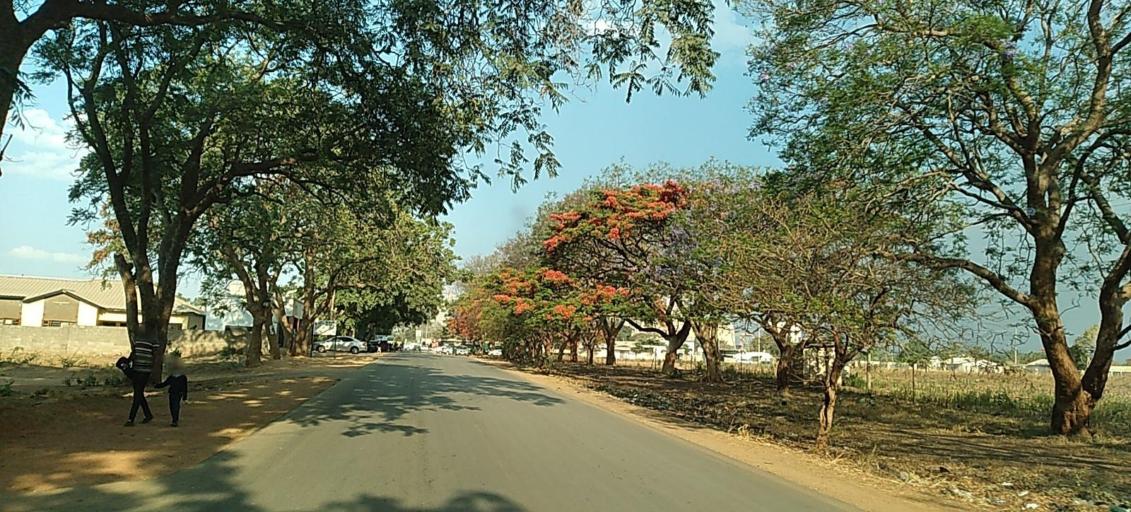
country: ZM
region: Lusaka
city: Lusaka
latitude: -15.5445
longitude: 28.2627
